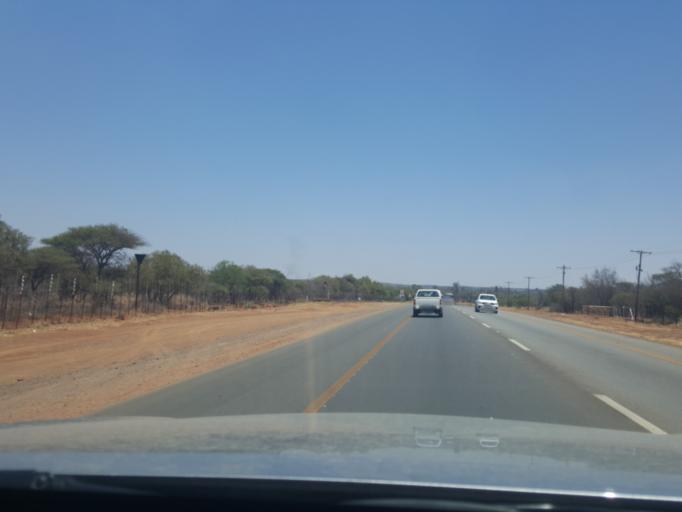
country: ZA
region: North-West
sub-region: Ngaka Modiri Molema District Municipality
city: Zeerust
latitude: -25.5566
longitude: 26.0671
